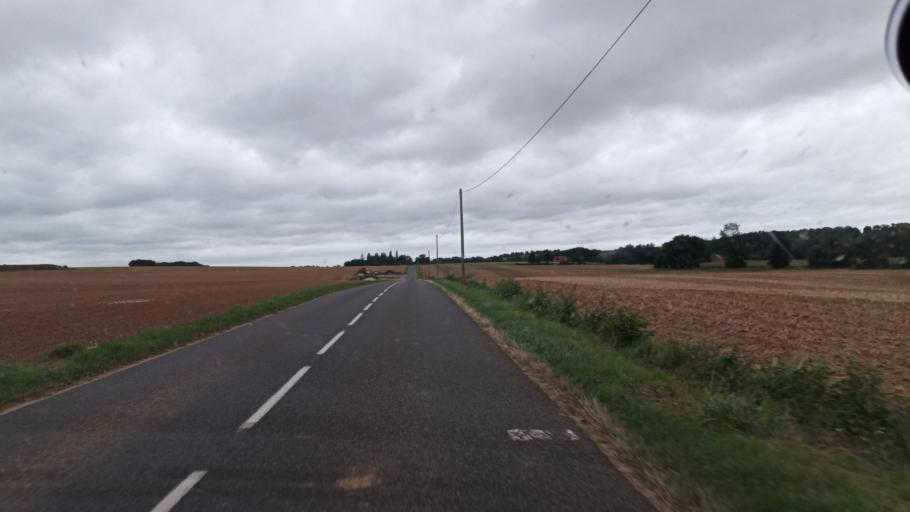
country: FR
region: Bourgogne
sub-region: Departement de l'Yonne
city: Cheroy
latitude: 48.2439
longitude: 3.0382
